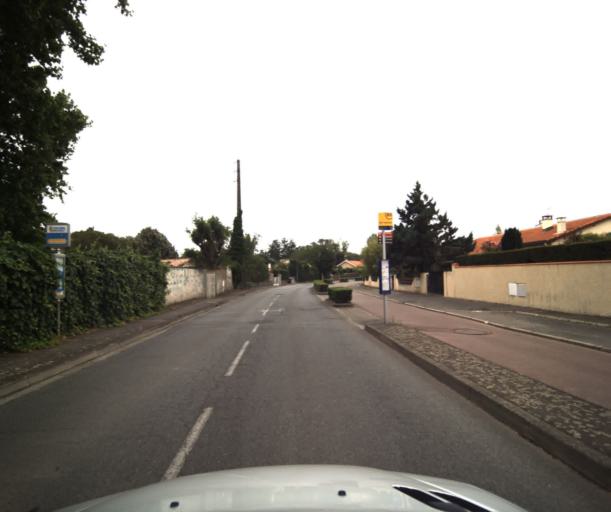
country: FR
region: Midi-Pyrenees
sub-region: Departement de la Haute-Garonne
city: Pinsaguel
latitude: 43.5148
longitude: 1.3927
